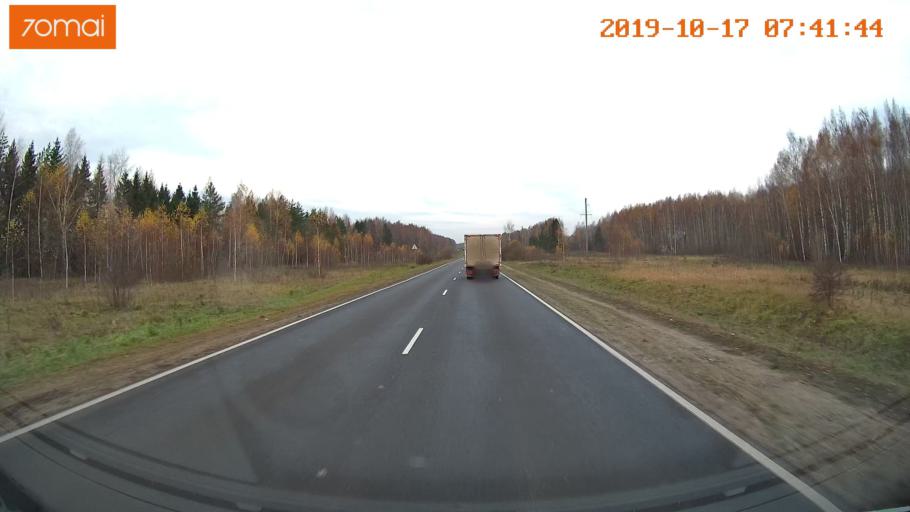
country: RU
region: Vladimir
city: Yur'yev-Pol'skiy
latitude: 56.4834
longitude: 39.8041
